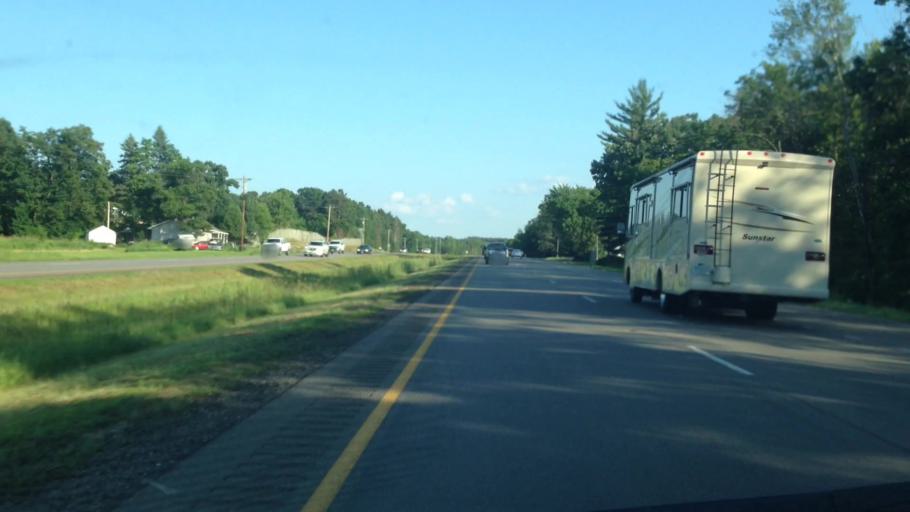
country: US
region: Minnesota
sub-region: Sherburne County
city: Zimmerman
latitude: 45.4265
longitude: -93.5719
